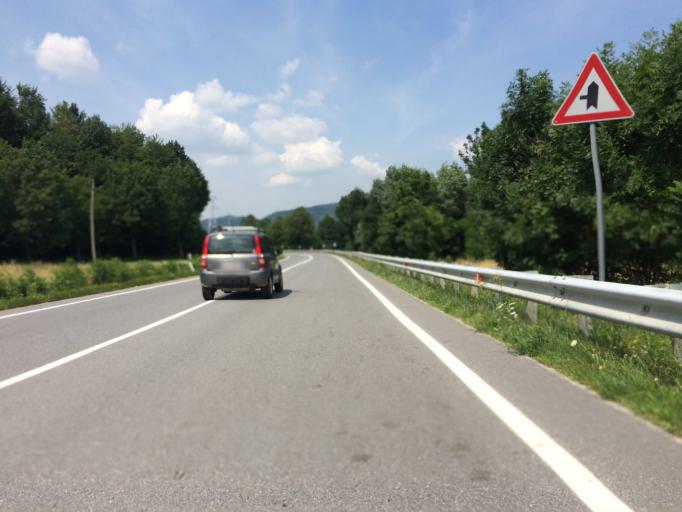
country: IT
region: Piedmont
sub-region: Provincia di Cuneo
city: Robilante
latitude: 44.2726
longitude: 7.5191
